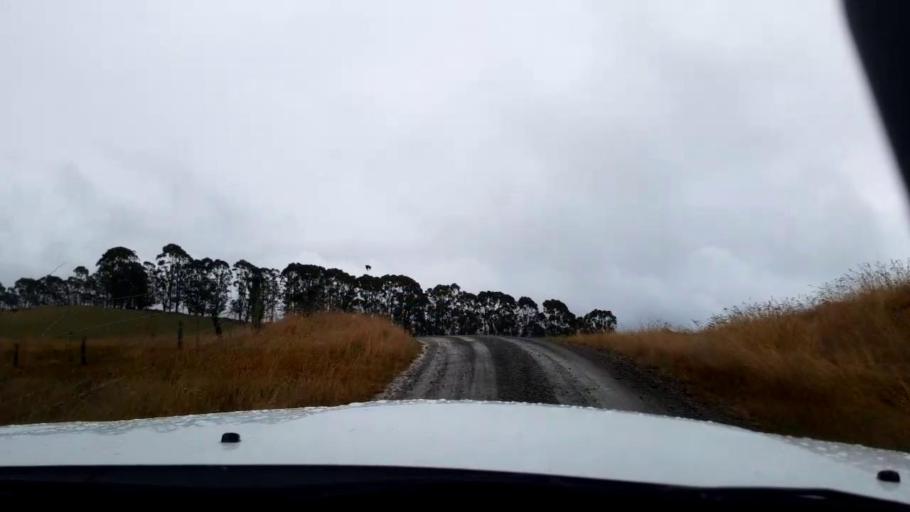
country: NZ
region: Canterbury
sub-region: Timaru District
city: Pleasant Point
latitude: -44.1728
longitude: 171.1085
